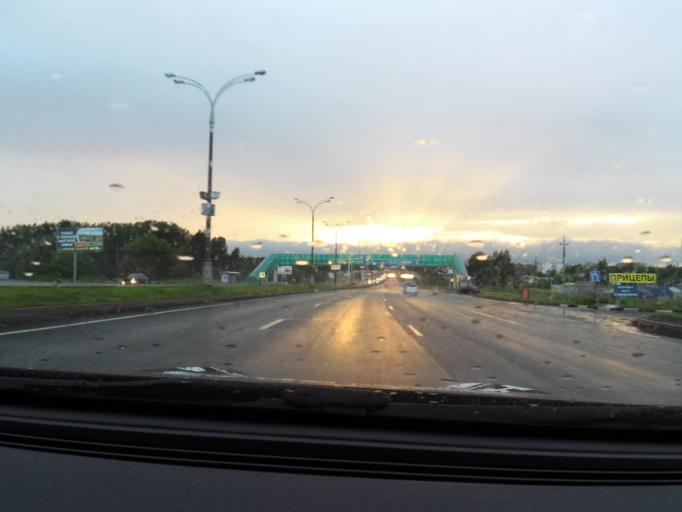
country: RU
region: Tatarstan
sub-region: Tukayevskiy Rayon
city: Naberezhnyye Chelny
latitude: 55.6676
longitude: 52.3024
